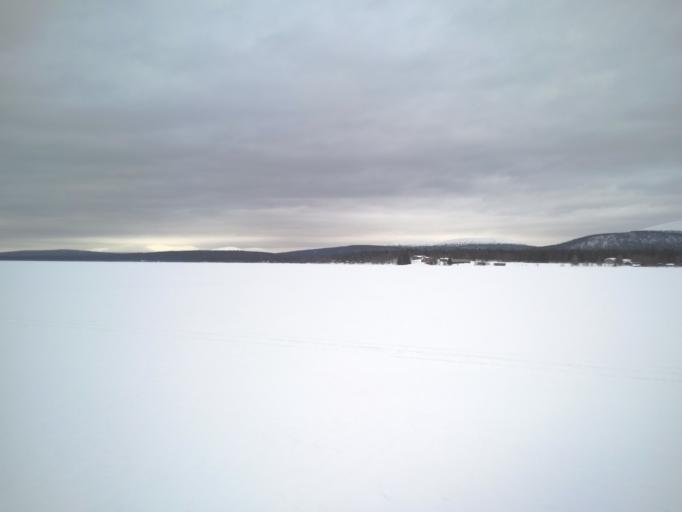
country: FI
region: Lapland
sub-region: Tunturi-Lappi
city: Muonio
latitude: 67.9189
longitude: 24.0394
